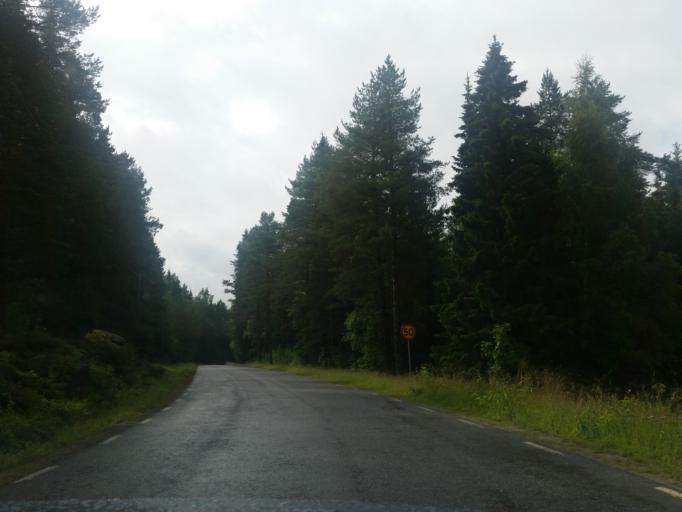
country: SE
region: Vaesterbotten
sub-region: Robertsfors Kommun
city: Robertsfors
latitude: 64.0369
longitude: 20.8513
